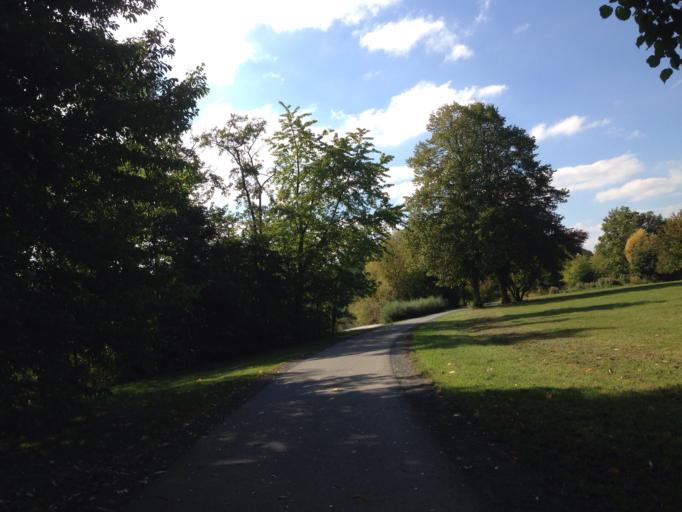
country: DE
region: Hesse
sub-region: Regierungsbezirk Giessen
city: Giessen
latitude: 50.5931
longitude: 8.6901
